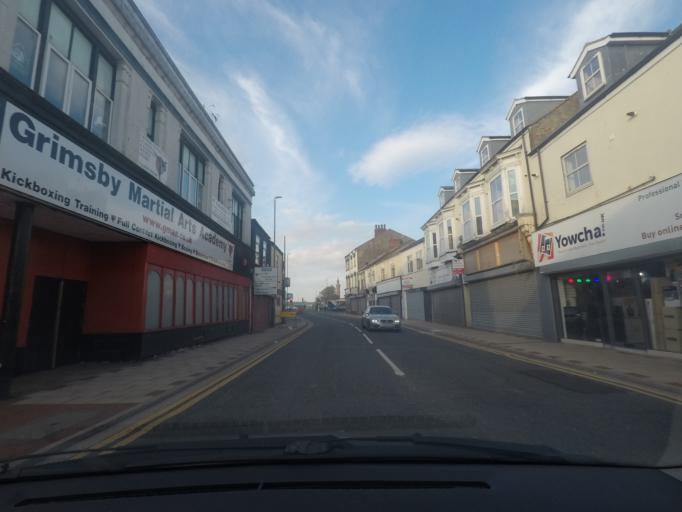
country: GB
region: England
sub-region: North East Lincolnshire
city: Grimsby
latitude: 53.5741
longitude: -0.0728
